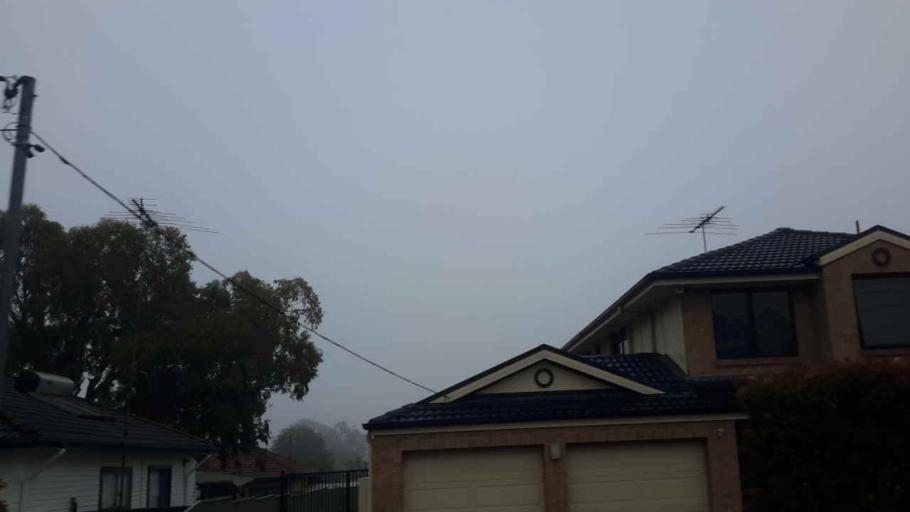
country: AU
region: New South Wales
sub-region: Penrith Municipality
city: Kingswood Park
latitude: -33.7617
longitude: 150.7104
